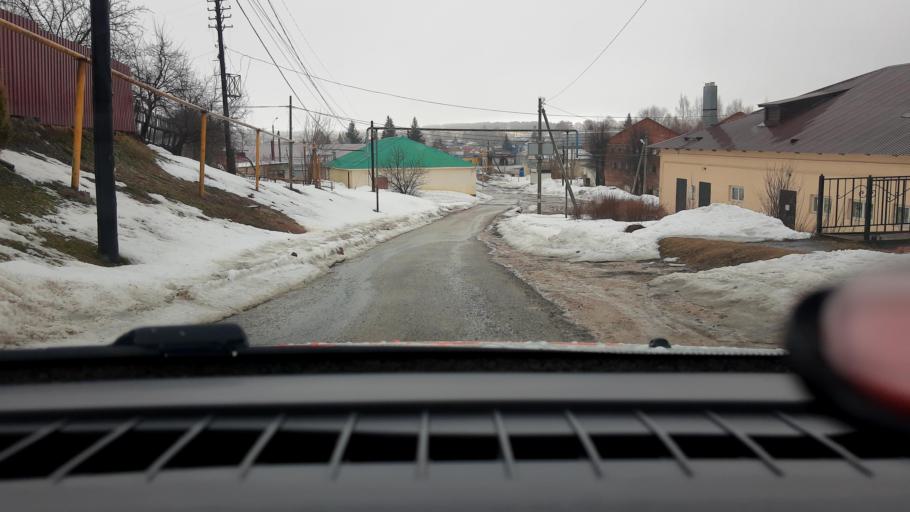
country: RU
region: Nizjnij Novgorod
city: Burevestnik
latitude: 56.1776
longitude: 43.7688
